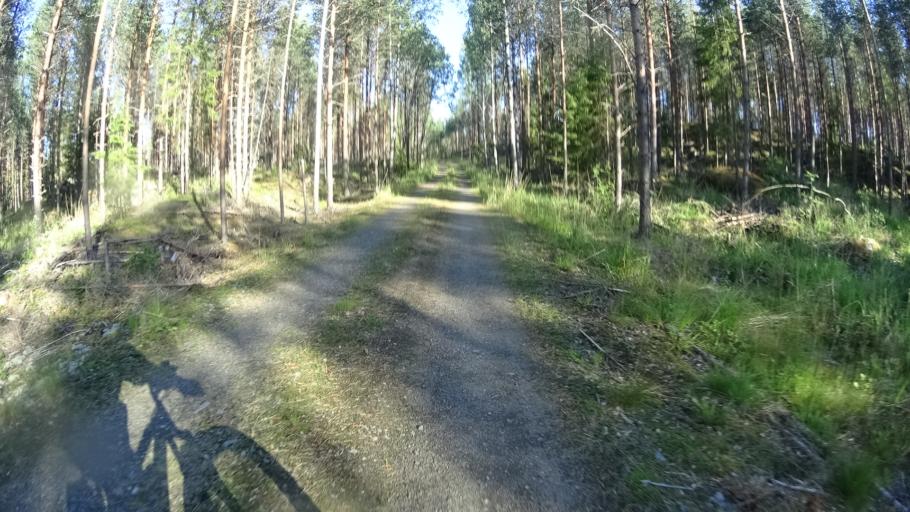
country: FI
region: Uusimaa
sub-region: Helsinki
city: Karkkila
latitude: 60.6656
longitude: 24.1295
